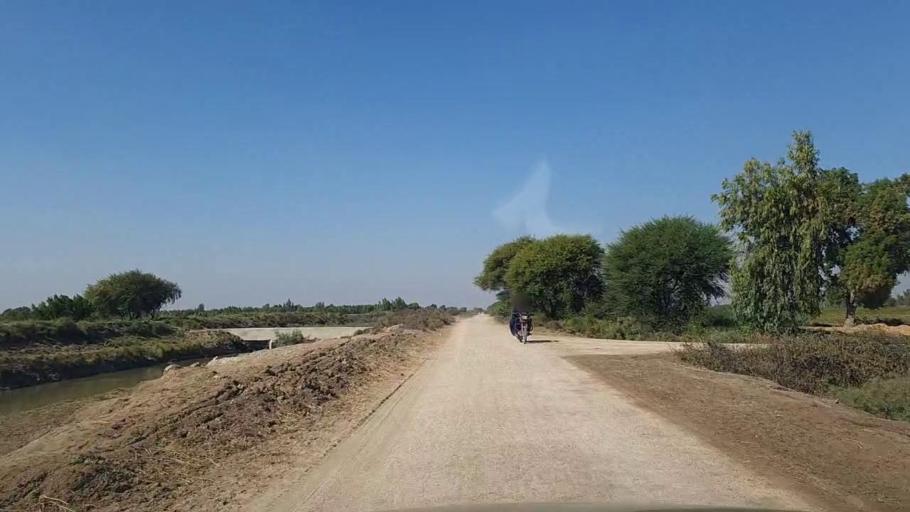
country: PK
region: Sindh
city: Mirpur Batoro
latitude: 24.7255
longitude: 68.2315
